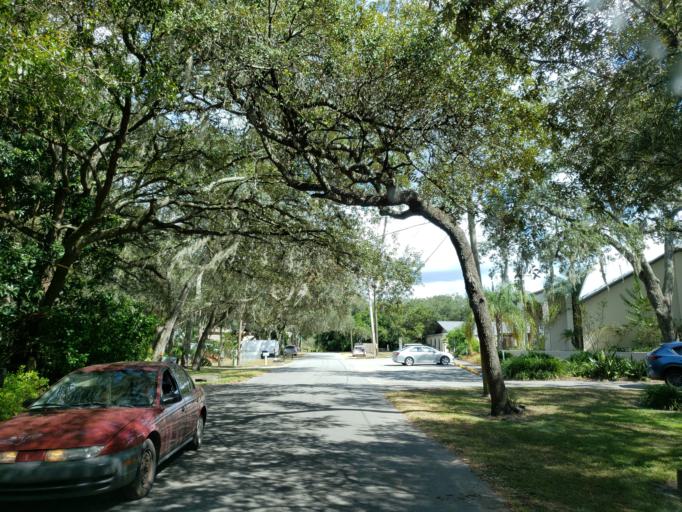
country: US
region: Florida
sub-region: Hillsborough County
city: Lake Magdalene
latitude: 28.0510
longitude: -82.4648
